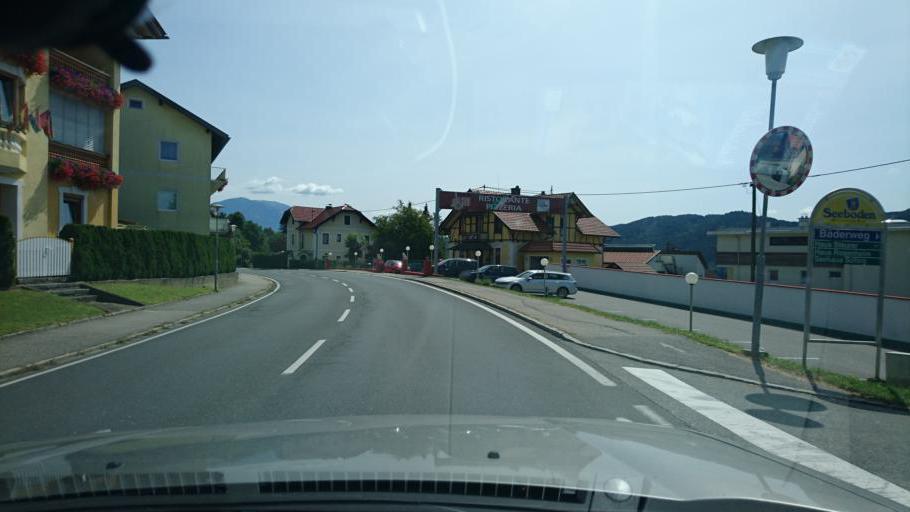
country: AT
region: Carinthia
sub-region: Politischer Bezirk Spittal an der Drau
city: Seeboden
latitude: 46.8183
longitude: 13.5237
